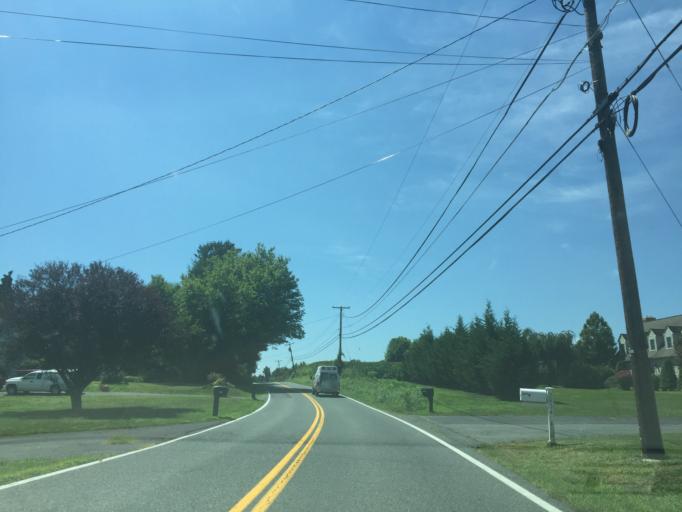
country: US
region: Maryland
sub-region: Harford County
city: Bel Air North
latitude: 39.6071
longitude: -76.3863
